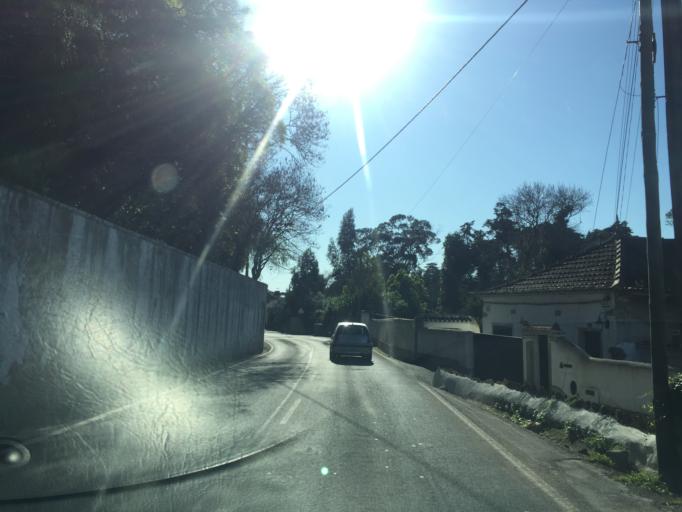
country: PT
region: Lisbon
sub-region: Sintra
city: Belas
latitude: 38.7787
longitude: -9.2655
